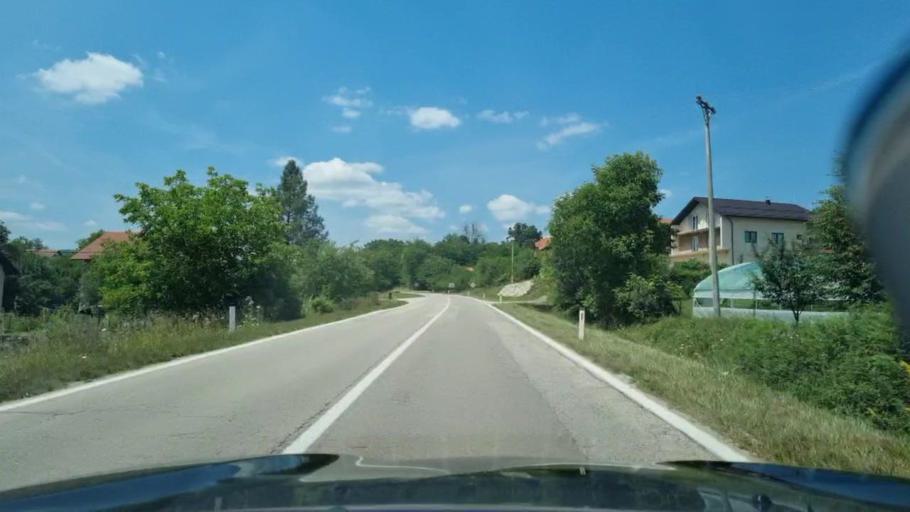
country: BA
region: Federation of Bosnia and Herzegovina
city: Velagici
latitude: 44.5602
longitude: 16.7263
